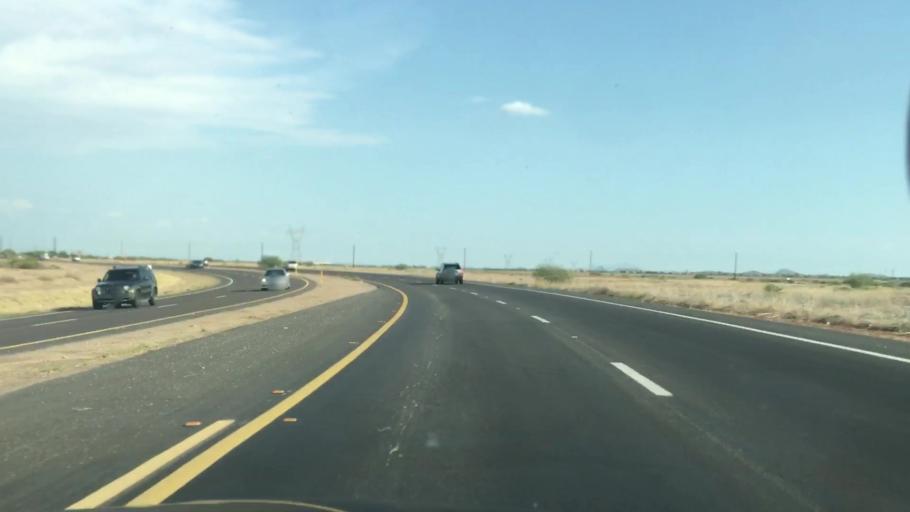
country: US
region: Arizona
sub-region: Pinal County
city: San Tan Valley
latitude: 33.1965
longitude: -111.5642
